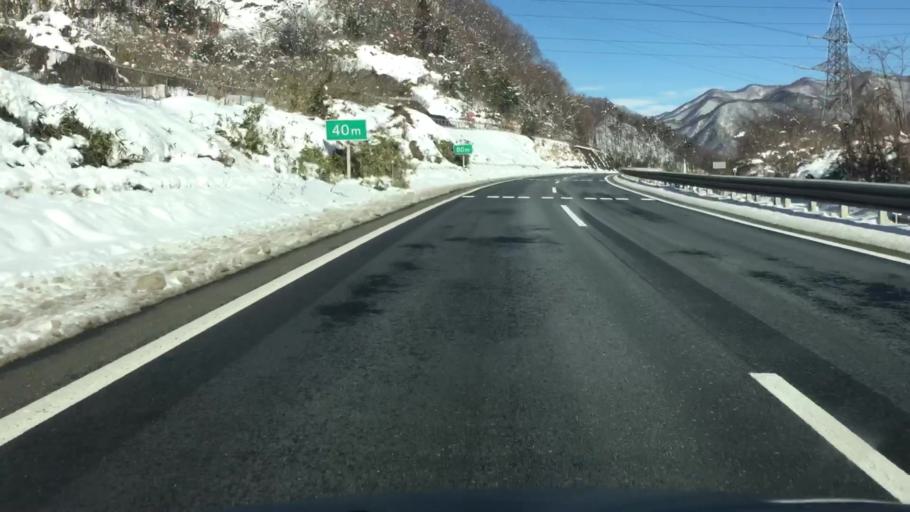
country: JP
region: Gunma
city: Numata
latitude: 36.7158
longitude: 138.9753
